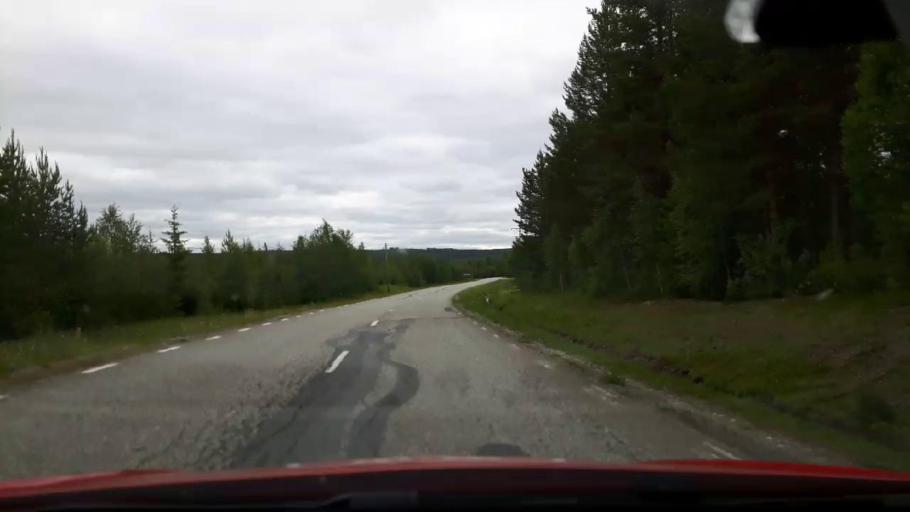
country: SE
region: Jaemtland
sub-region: Stroemsunds Kommun
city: Stroemsund
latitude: 63.3079
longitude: 15.7605
